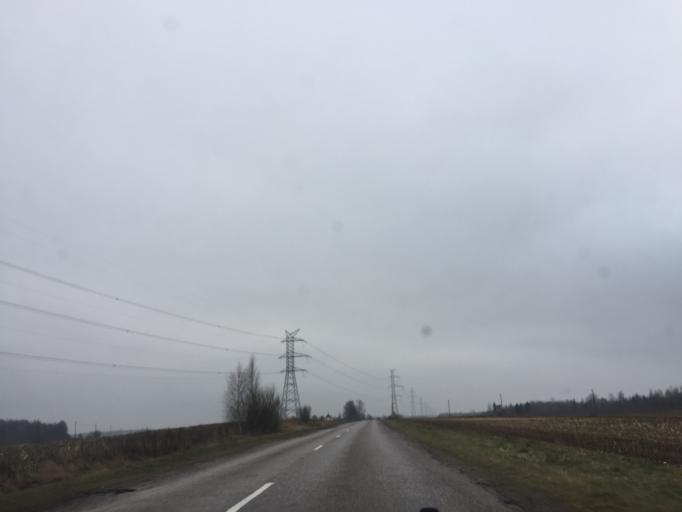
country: LV
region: Limbazu Rajons
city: Limbazi
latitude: 57.5769
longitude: 24.6628
